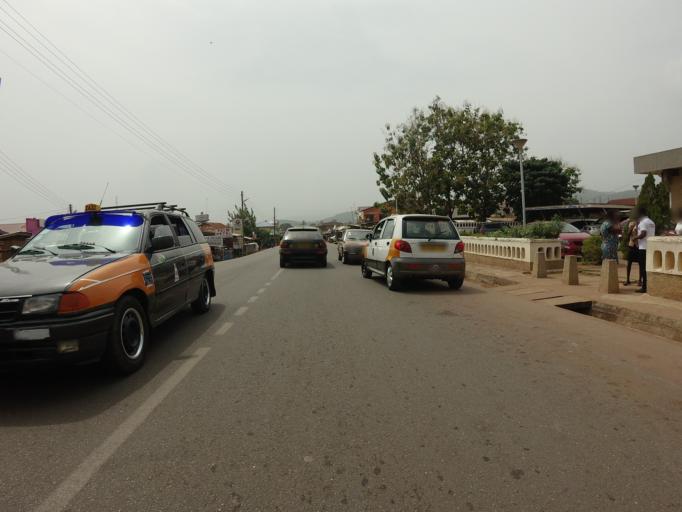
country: GH
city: Akropong
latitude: 6.1018
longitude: -0.0162
